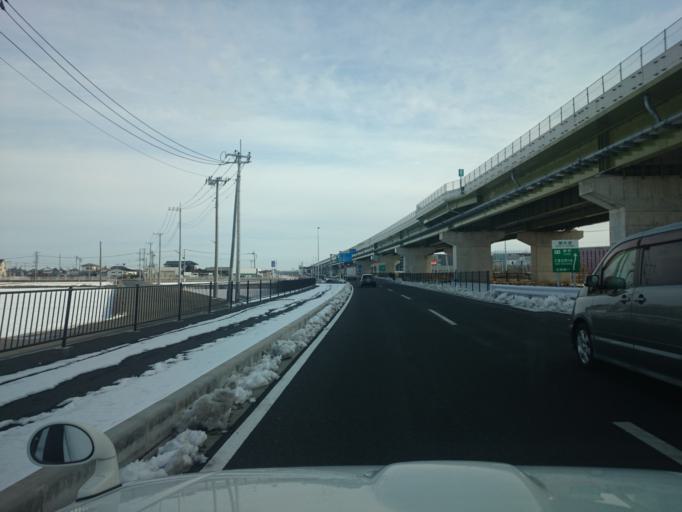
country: JP
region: Saitama
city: Satte
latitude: 36.0648
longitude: 139.7383
